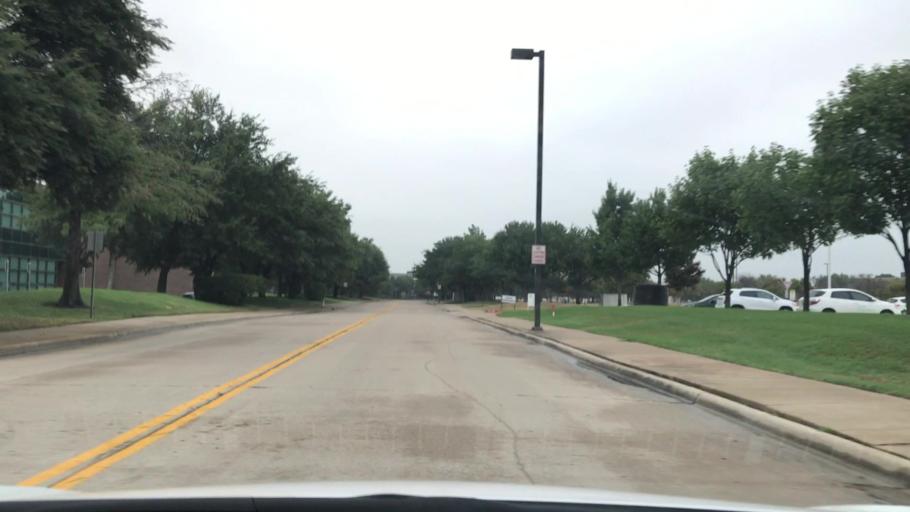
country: US
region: Texas
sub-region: Dallas County
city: Coppell
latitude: 32.9322
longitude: -97.0143
